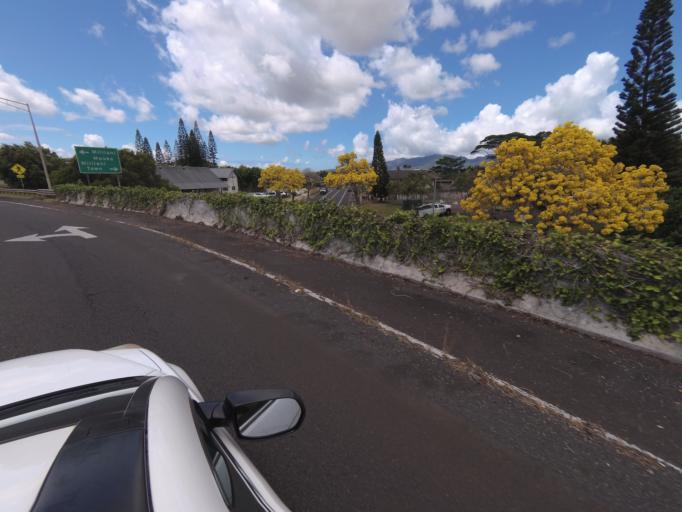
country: US
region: Hawaii
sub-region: Honolulu County
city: Waipi'o Acres
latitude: 21.4655
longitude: -158.0057
